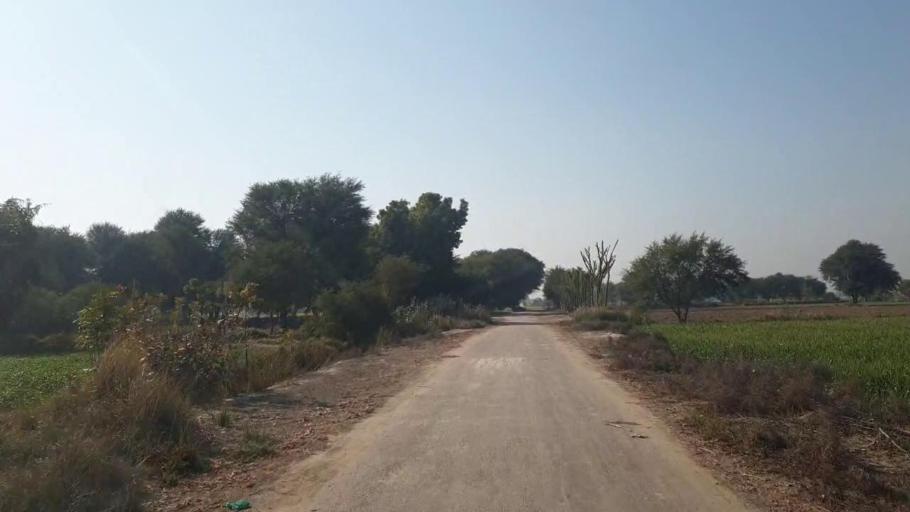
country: PK
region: Sindh
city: Shahpur Chakar
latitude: 26.0799
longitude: 68.5851
